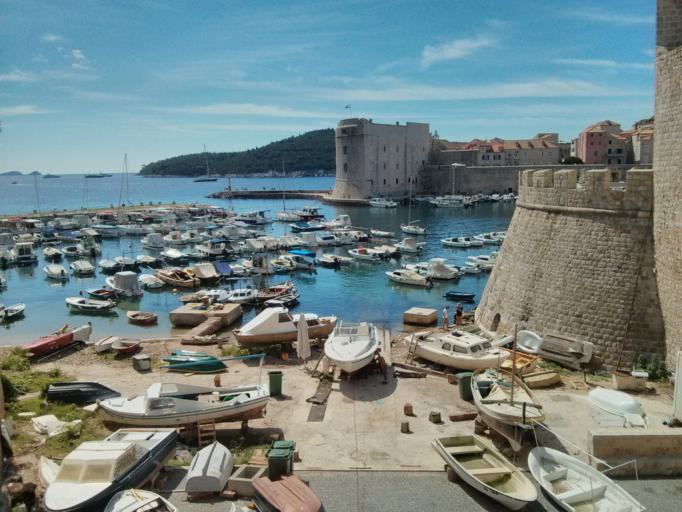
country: HR
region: Dubrovacko-Neretvanska
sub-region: Grad Dubrovnik
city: Dubrovnik
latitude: 42.6419
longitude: 18.1120
